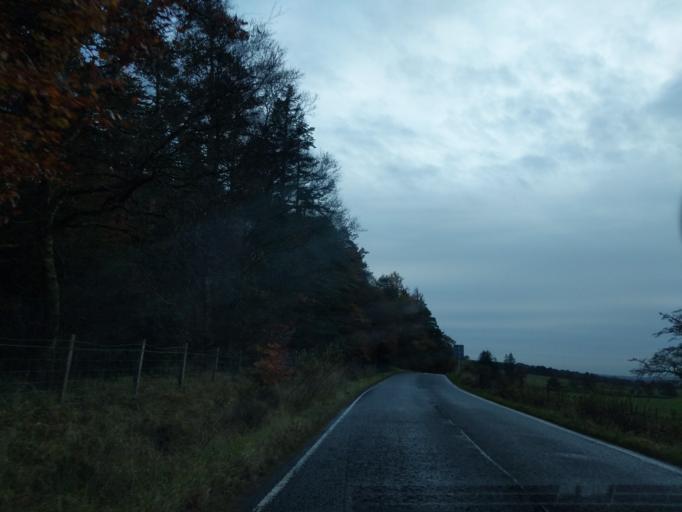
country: GB
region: Scotland
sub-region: West Lothian
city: Linlithgow
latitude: 55.9444
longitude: -3.6171
